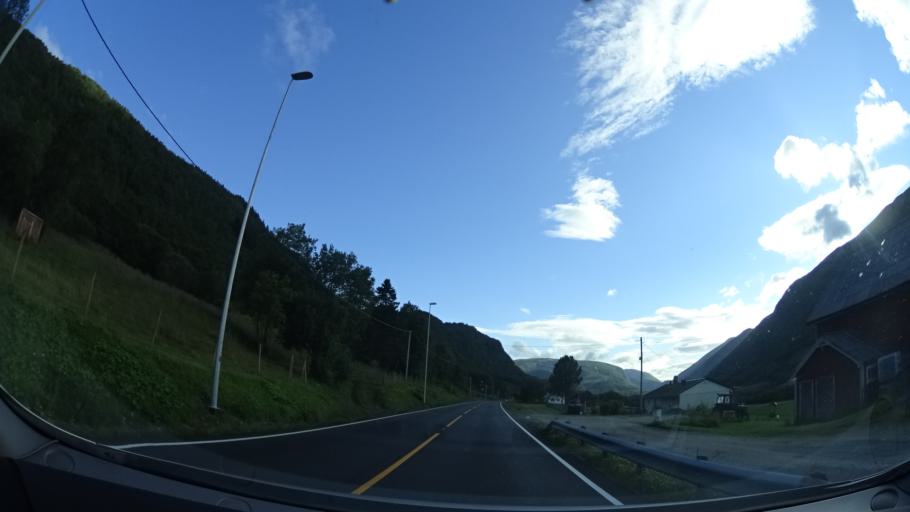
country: NO
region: More og Romsdal
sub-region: Gjemnes
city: Batnfjordsora
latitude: 62.8713
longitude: 7.6343
